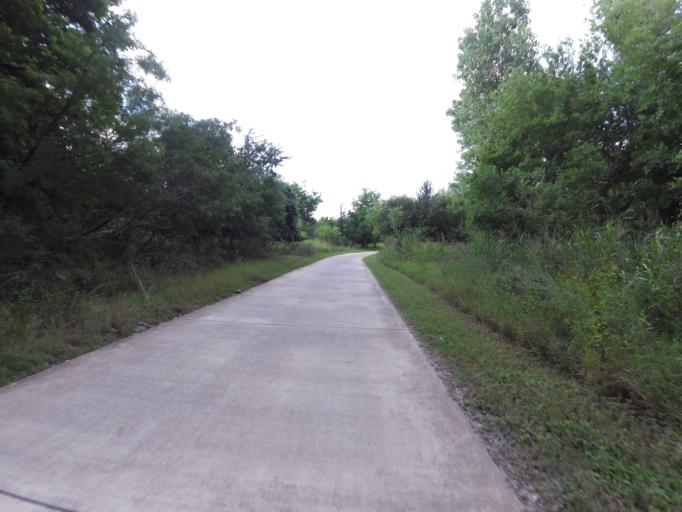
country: US
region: Texas
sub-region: Bexar County
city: Leon Valley
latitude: 29.5054
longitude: -98.6371
